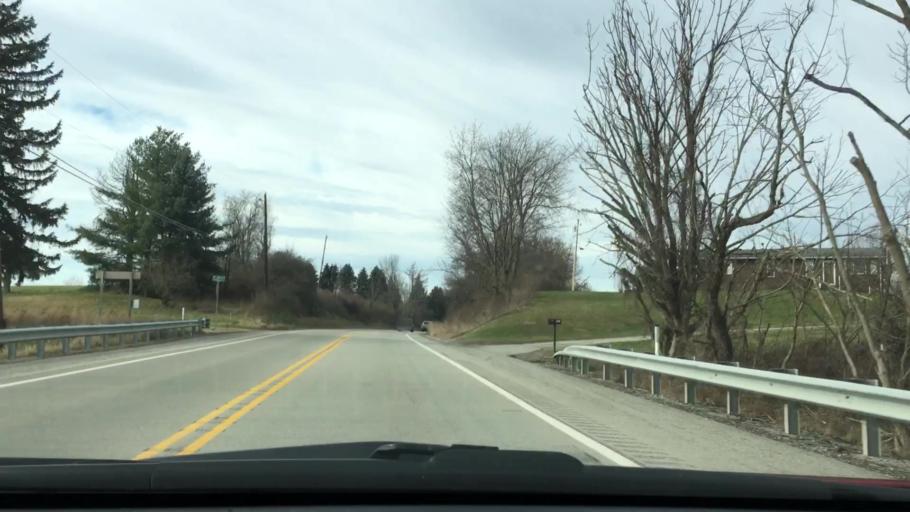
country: US
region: Pennsylvania
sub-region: Fayette County
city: South Uniontown
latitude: 39.8926
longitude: -79.8072
